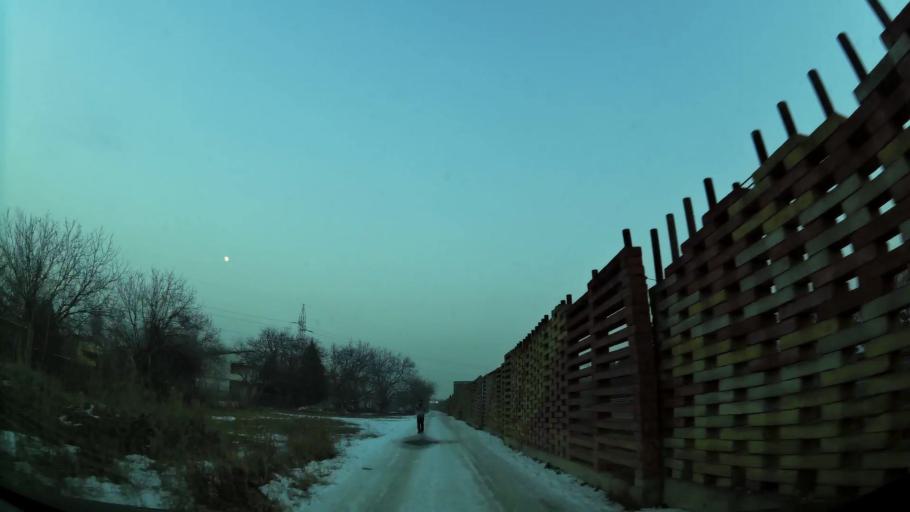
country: MK
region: Kisela Voda
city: Kisela Voda
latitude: 41.9985
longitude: 21.5052
